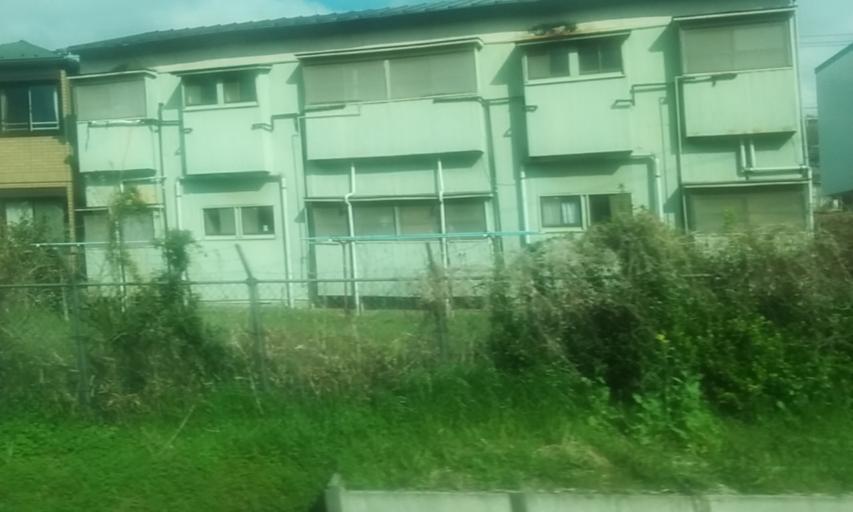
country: JP
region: Kanagawa
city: Yokohama
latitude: 35.4449
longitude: 139.5732
